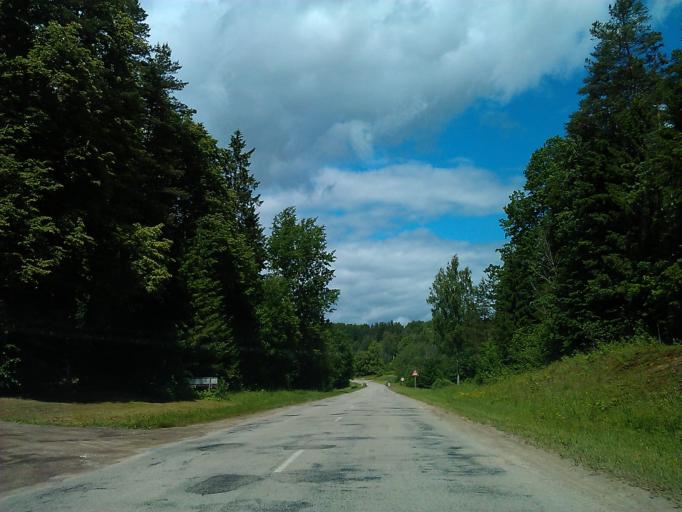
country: LV
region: Talsu Rajons
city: Sabile
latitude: 57.0821
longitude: 22.5267
